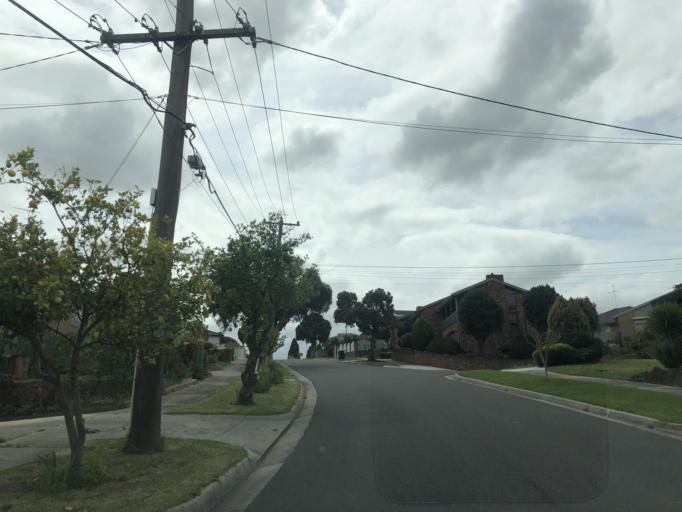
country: AU
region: Victoria
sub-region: Greater Dandenong
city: Noble Park North
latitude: -37.9458
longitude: 145.2118
